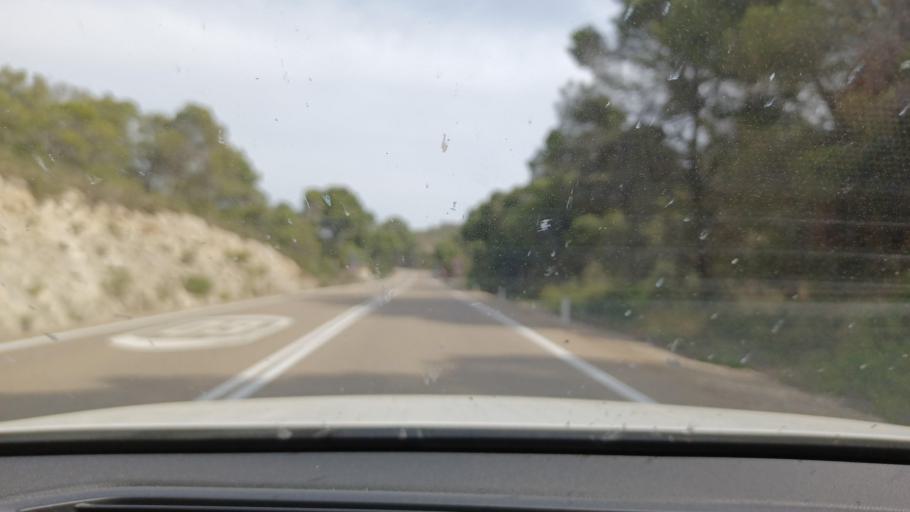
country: ES
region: Aragon
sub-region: Provincia de Zaragoza
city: Chiprana
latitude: 41.3548
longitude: -0.0998
